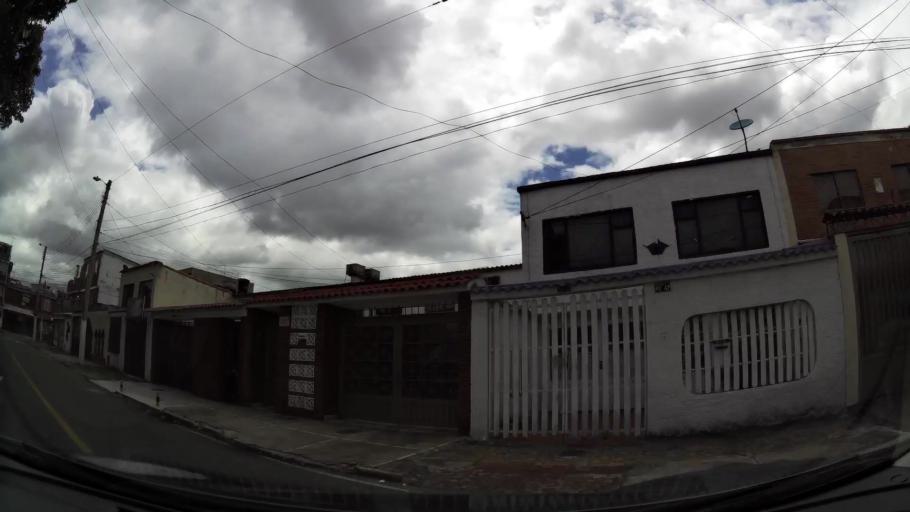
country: CO
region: Bogota D.C.
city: Barrio San Luis
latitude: 4.7056
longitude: -74.0962
